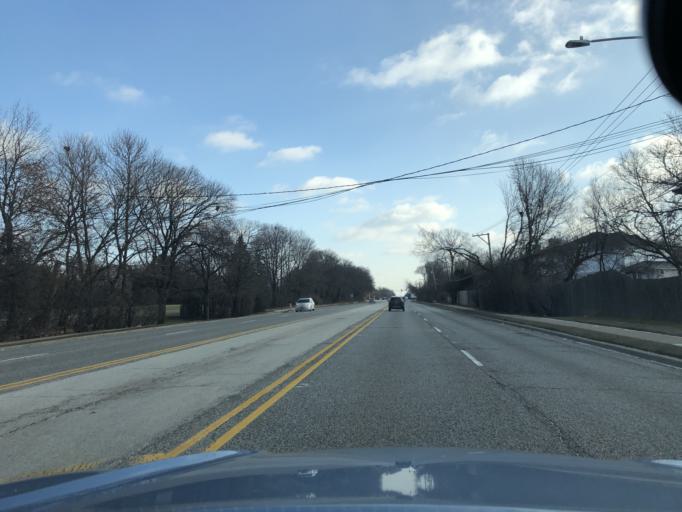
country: US
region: Illinois
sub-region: Cook County
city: Northbrook
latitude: 42.1058
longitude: -87.8534
